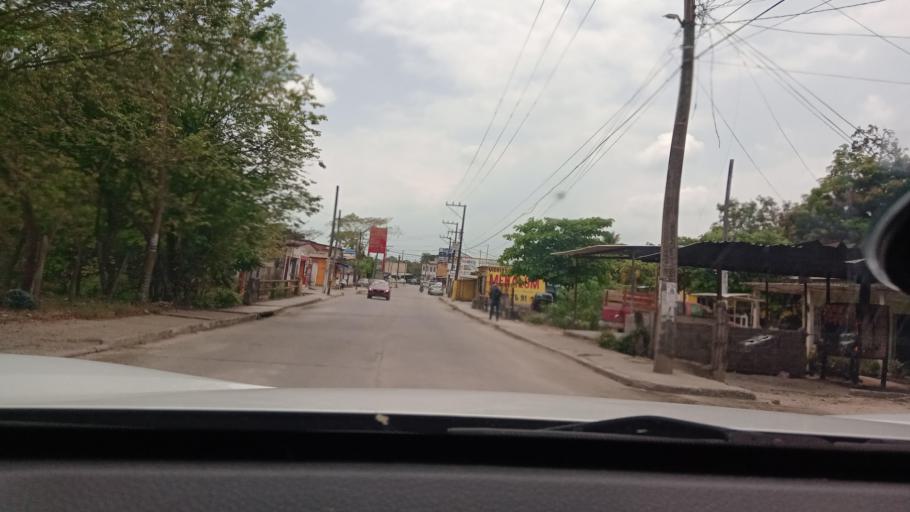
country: MX
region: Veracruz
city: Las Choapas
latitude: 17.9004
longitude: -94.0978
